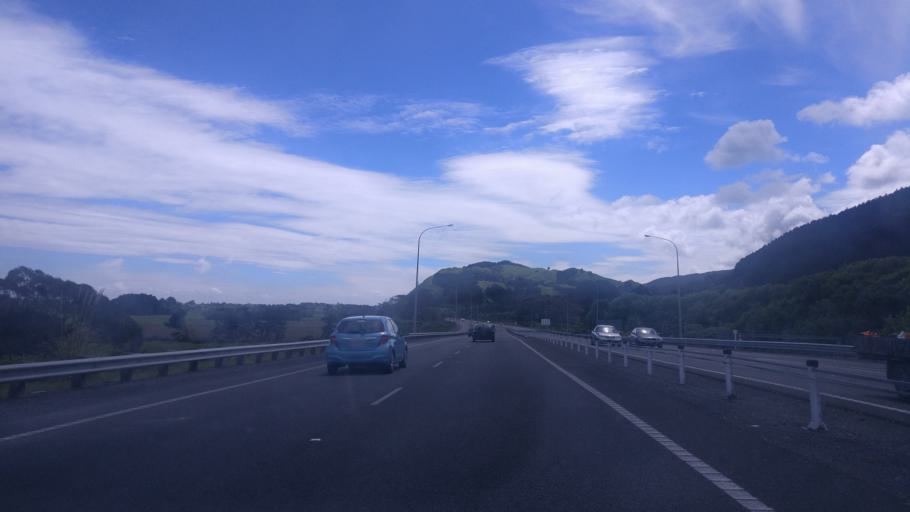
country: NZ
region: Wellington
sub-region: Kapiti Coast District
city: Paraparaumu
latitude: -40.9689
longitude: 174.9841
